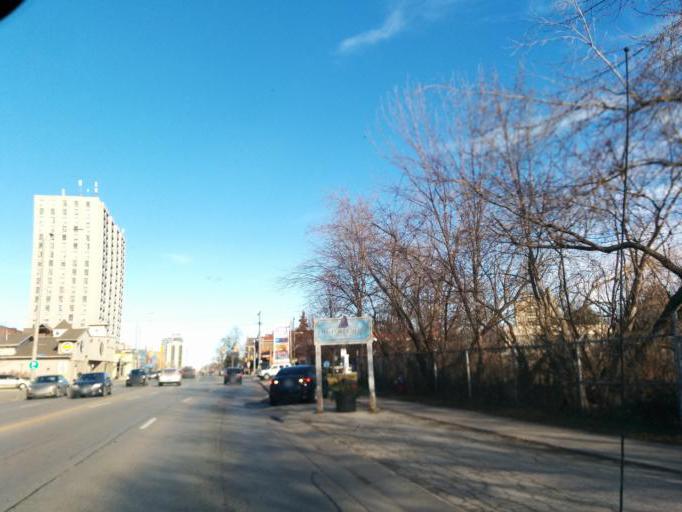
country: CA
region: Ontario
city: Mississauga
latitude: 43.5471
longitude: -79.5907
